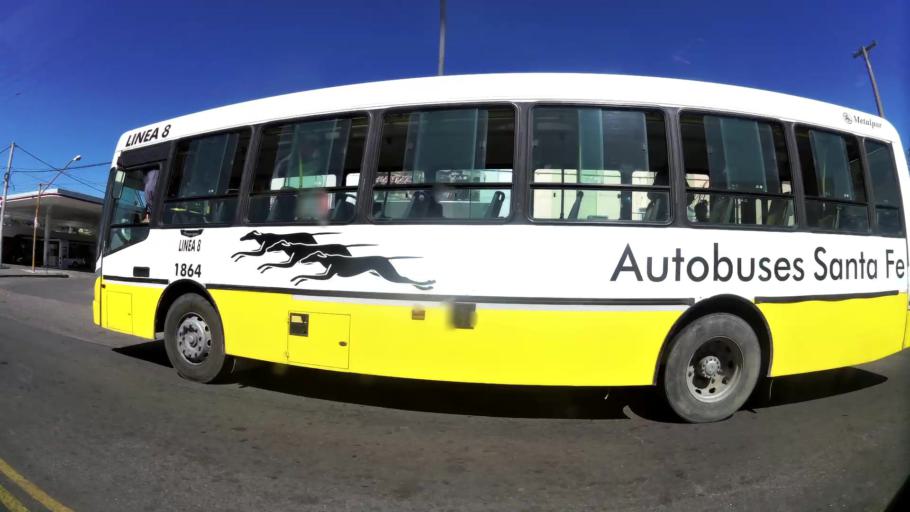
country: AR
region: Santa Fe
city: Santa Fe de la Vera Cruz
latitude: -31.6033
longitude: -60.6751
